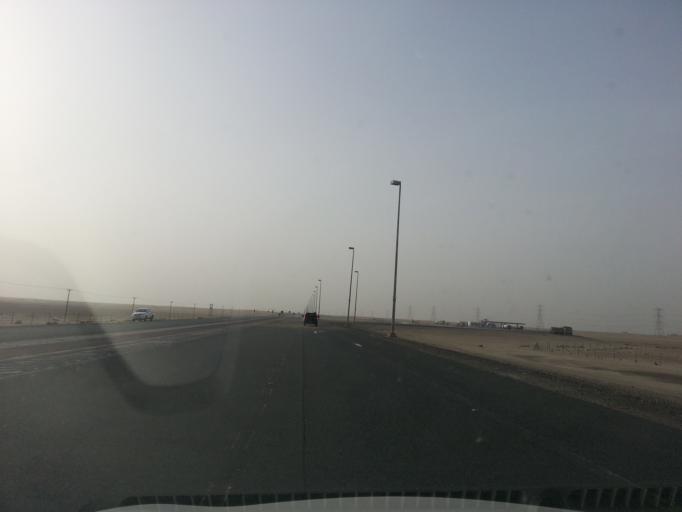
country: AE
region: Dubai
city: Dubai
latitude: 24.8005
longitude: 55.0714
